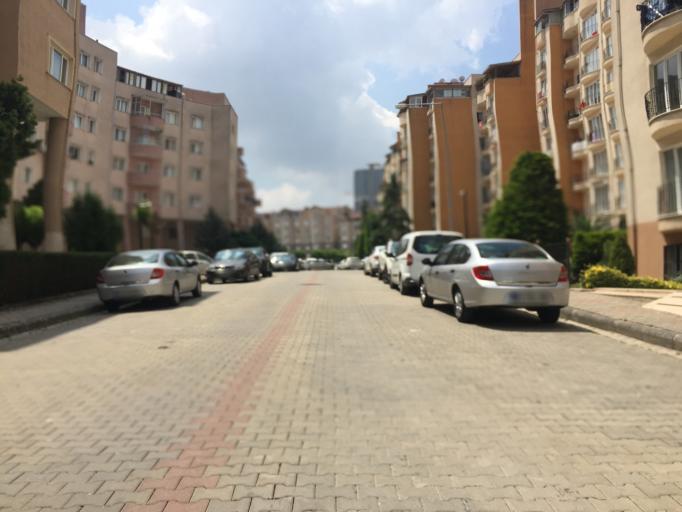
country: TR
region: Istanbul
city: Esenyurt
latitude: 41.0748
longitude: 28.6643
